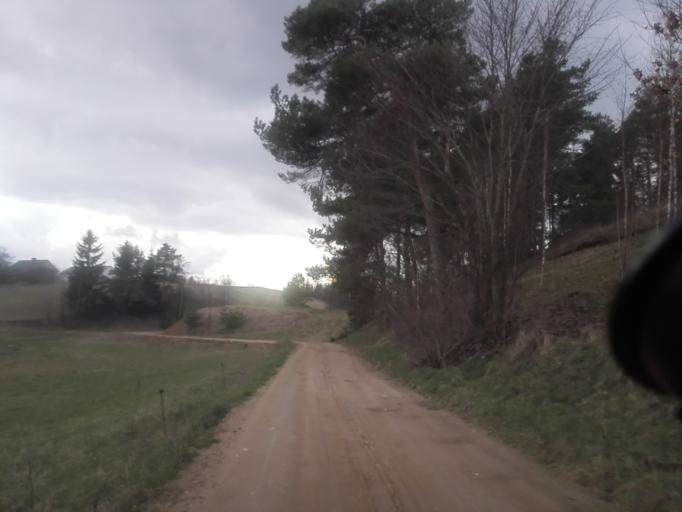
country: PL
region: Podlasie
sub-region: Suwalki
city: Suwalki
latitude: 54.2583
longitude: 22.9552
